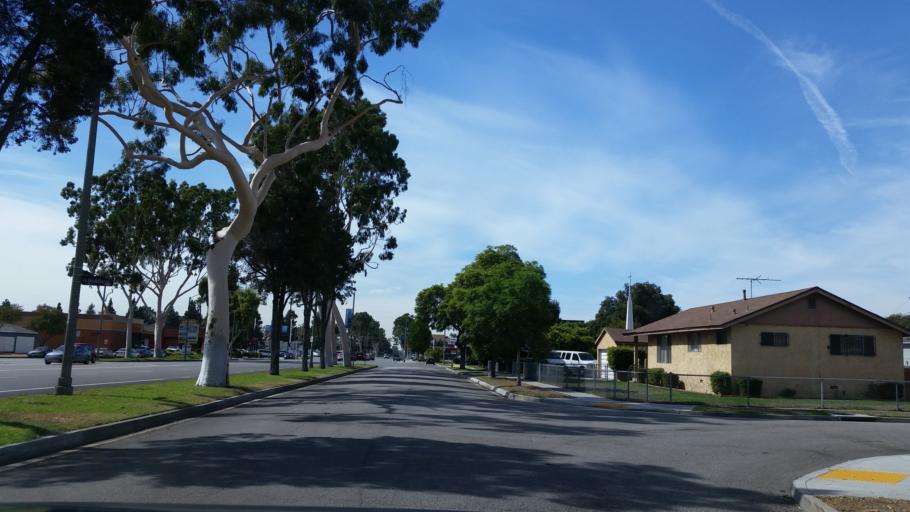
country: US
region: California
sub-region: Los Angeles County
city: Lakewood
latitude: 33.8604
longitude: -118.1399
